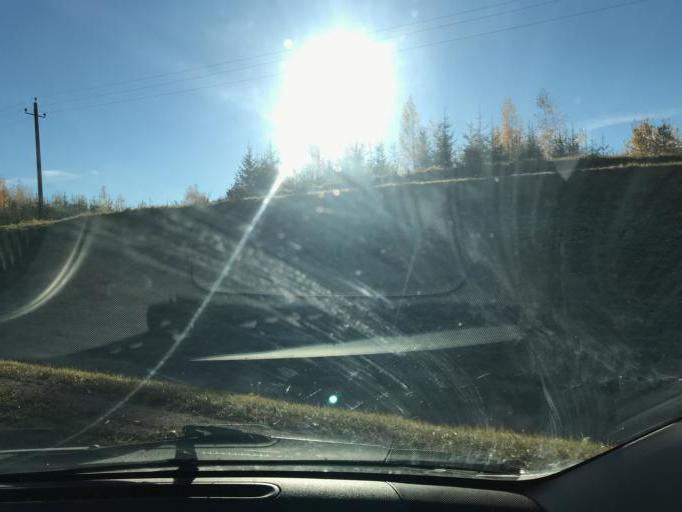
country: BY
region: Vitebsk
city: Vitebsk
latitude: 55.1032
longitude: 30.2909
